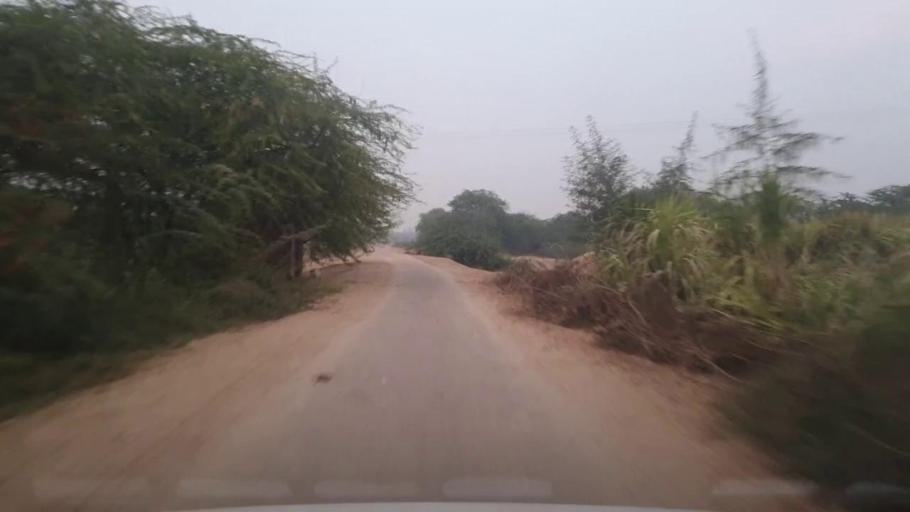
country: PK
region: Sindh
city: Gambat
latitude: 27.3437
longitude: 68.6108
